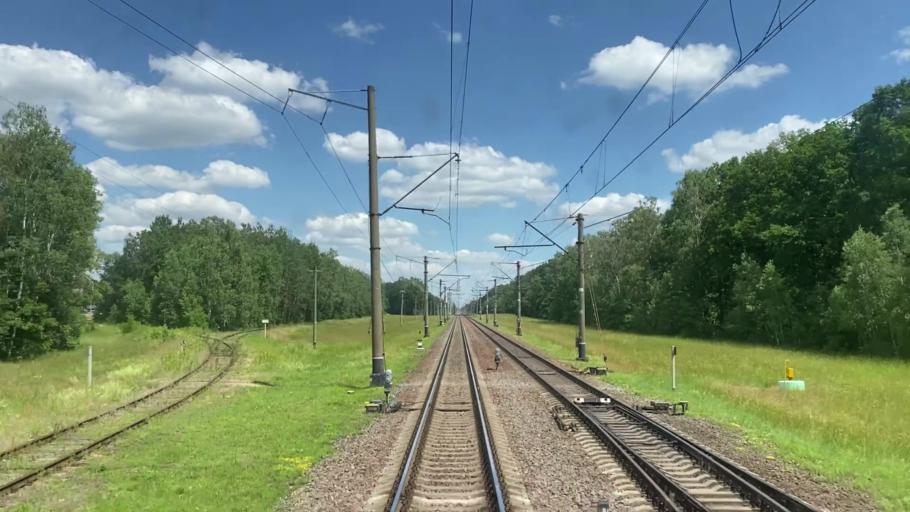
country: BY
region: Brest
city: Pruzhany
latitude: 52.4790
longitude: 24.5505
